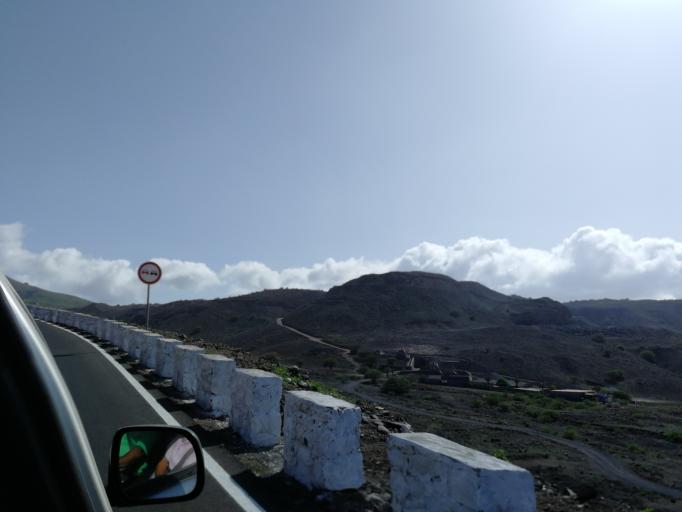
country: CV
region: Sao Vicente
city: Mindelo
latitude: 16.8861
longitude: -24.9413
